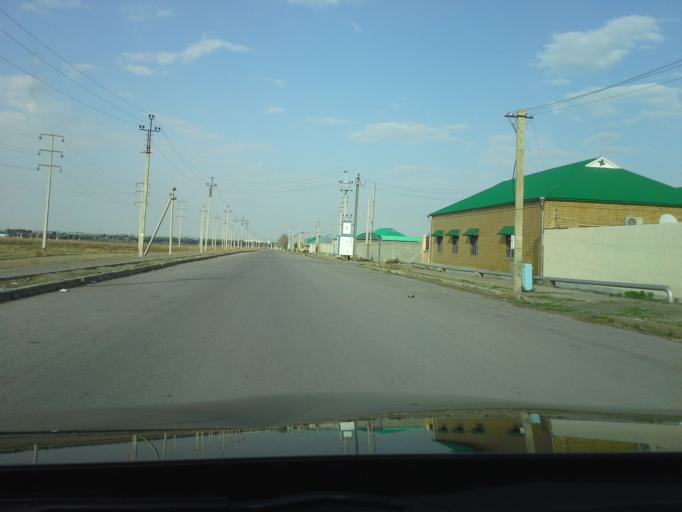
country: TM
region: Ahal
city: Abadan
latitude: 38.0232
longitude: 58.2185
